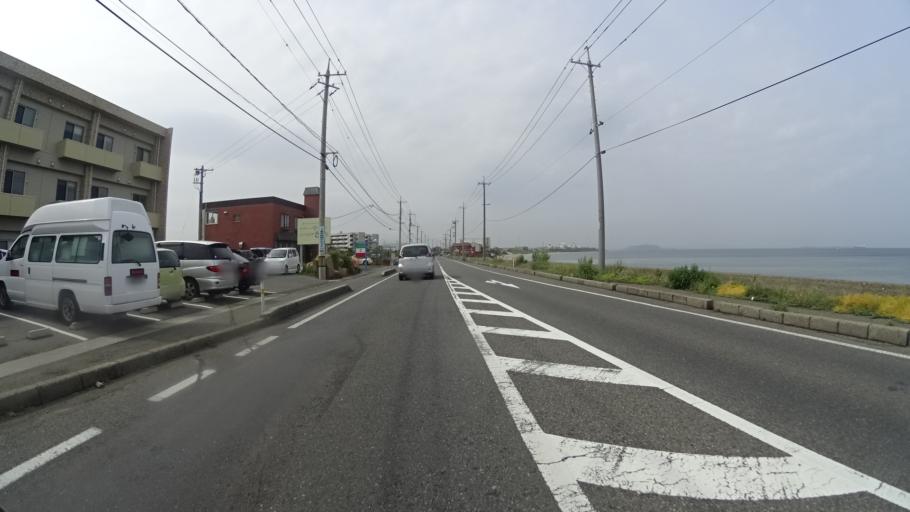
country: JP
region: Yamaguchi
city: Shimonoseki
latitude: 34.0462
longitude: 130.9151
